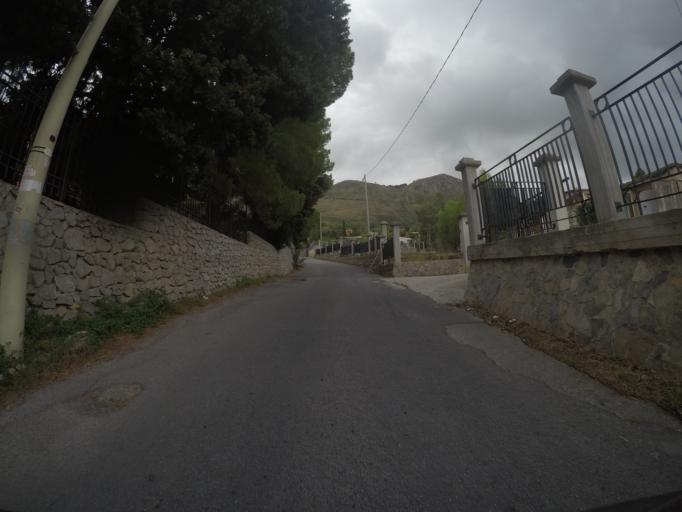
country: IT
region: Sicily
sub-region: Palermo
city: Carini
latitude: 38.1261
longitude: 13.1823
